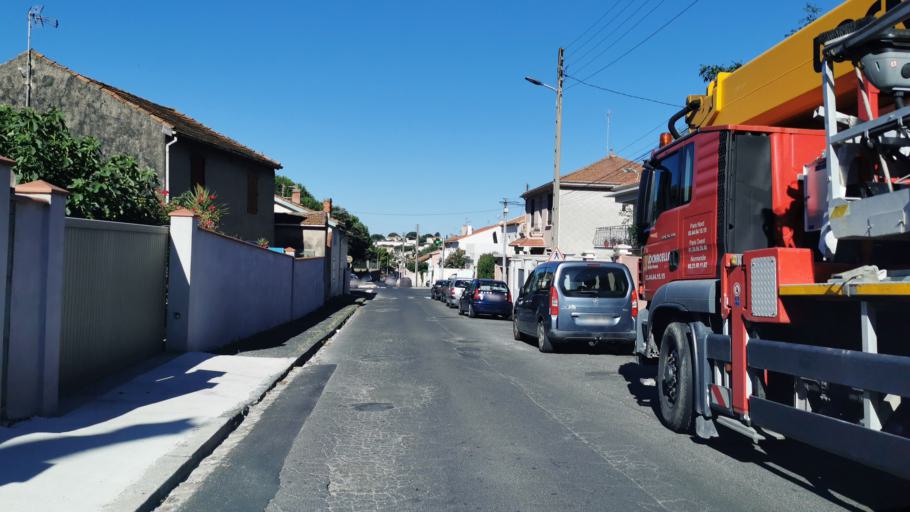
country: FR
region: Languedoc-Roussillon
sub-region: Departement de l'Herault
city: Beziers
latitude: 43.3531
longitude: 3.2178
